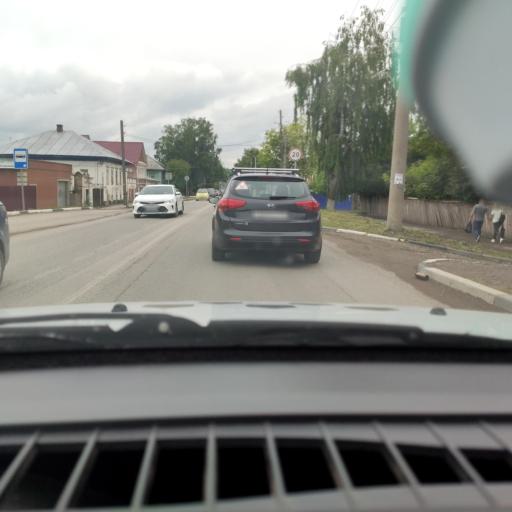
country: RU
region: Perm
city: Kungur
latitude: 57.4331
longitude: 56.9434
